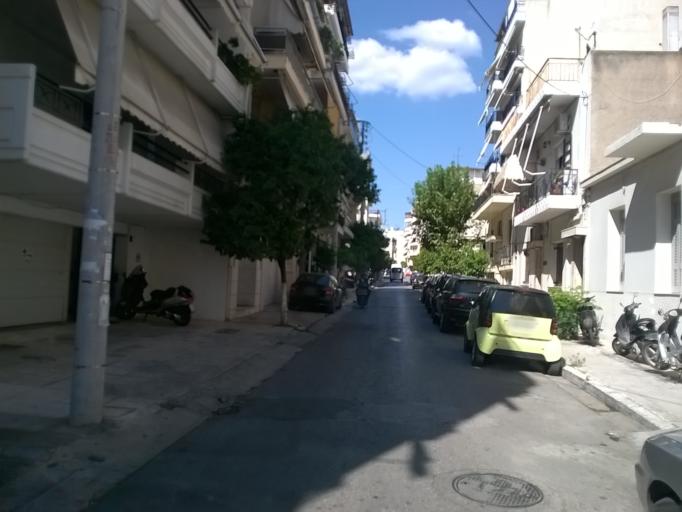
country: GR
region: Attica
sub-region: Nomos Piraios
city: Nikaia
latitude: 37.9637
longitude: 23.6530
